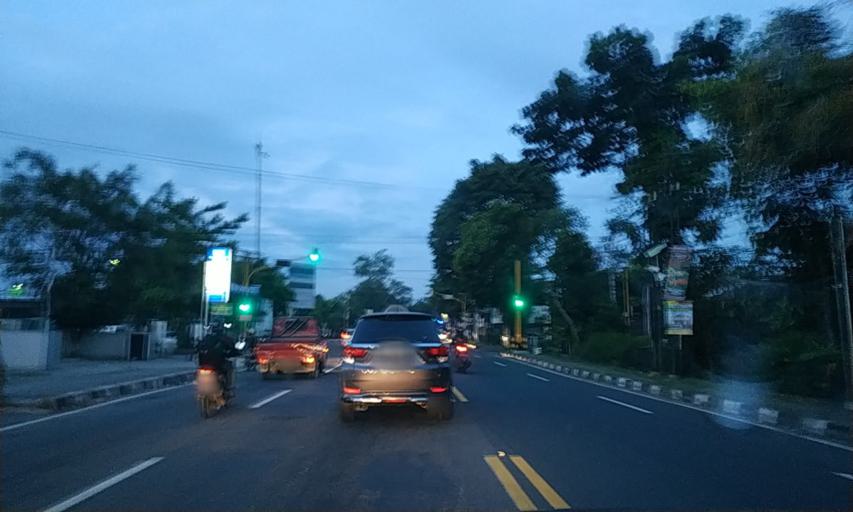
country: ID
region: Daerah Istimewa Yogyakarta
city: Godean
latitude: -7.8270
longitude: 110.2240
